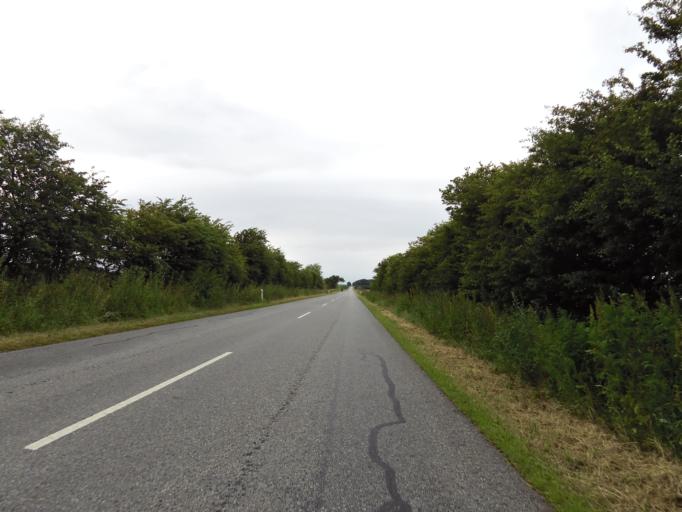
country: DK
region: South Denmark
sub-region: Tonder Kommune
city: Logumkloster
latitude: 55.1274
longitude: 8.9664
